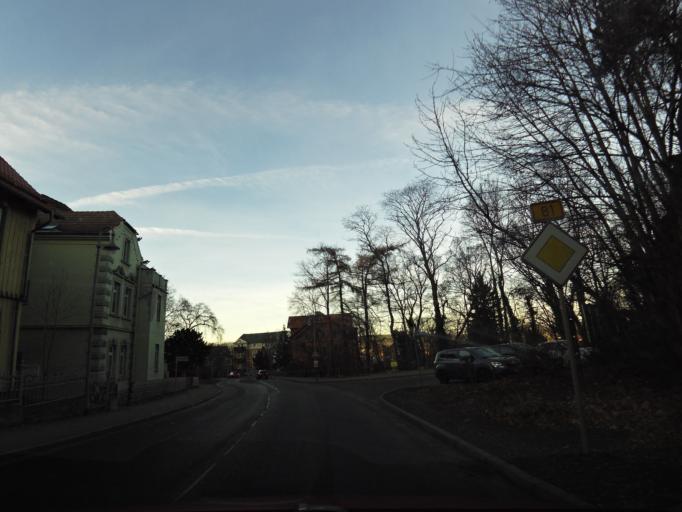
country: DE
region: Saxony-Anhalt
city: Blankenburg
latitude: 51.7883
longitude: 10.9617
